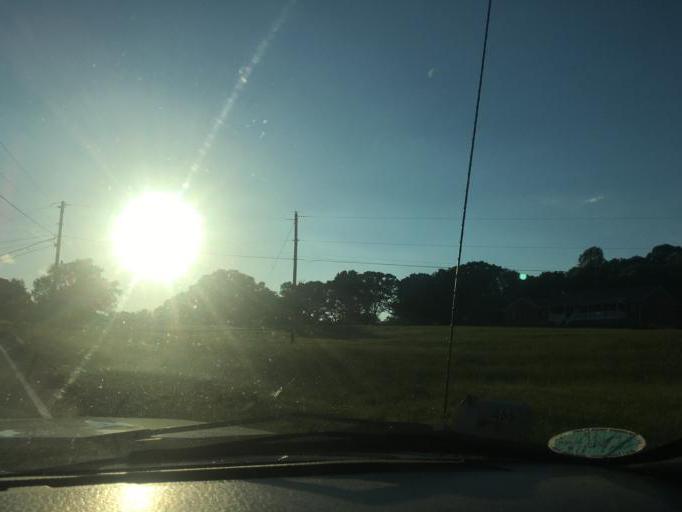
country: US
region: Georgia
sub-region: Dawson County
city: Dawsonville
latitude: 34.3360
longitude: -84.1266
